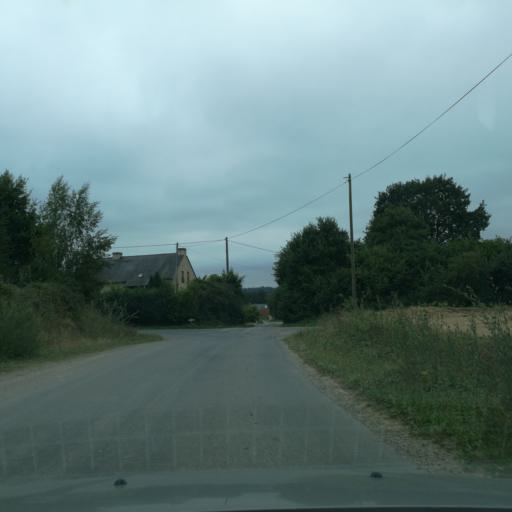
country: FR
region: Brittany
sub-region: Departement d'Ille-et-Vilaine
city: Montauban-de-Bretagne
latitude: 48.1860
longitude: -2.0186
